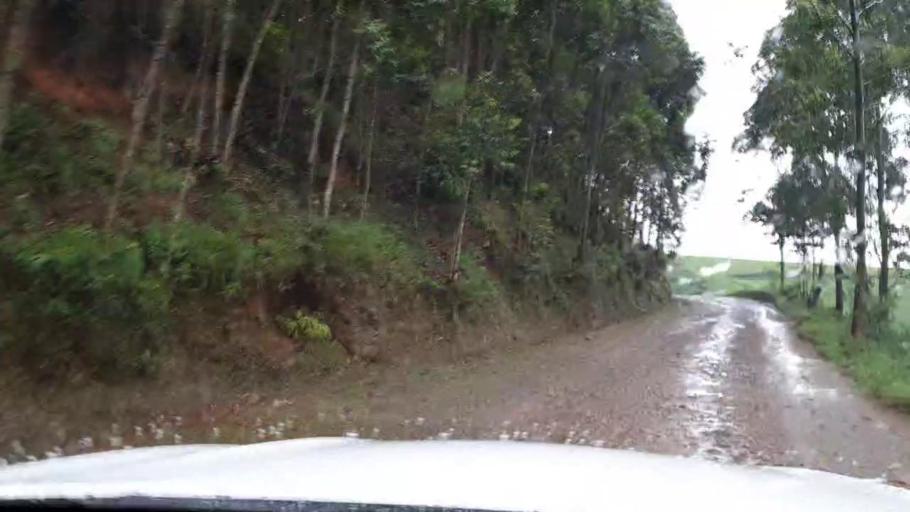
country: RW
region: Western Province
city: Cyangugu
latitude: -2.4595
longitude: 29.0369
